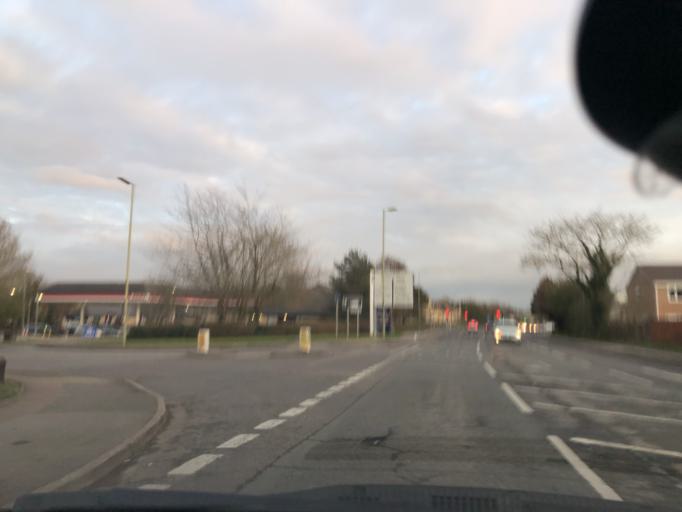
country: GB
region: England
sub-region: Oxfordshire
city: Witney
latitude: 51.7786
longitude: -1.4936
